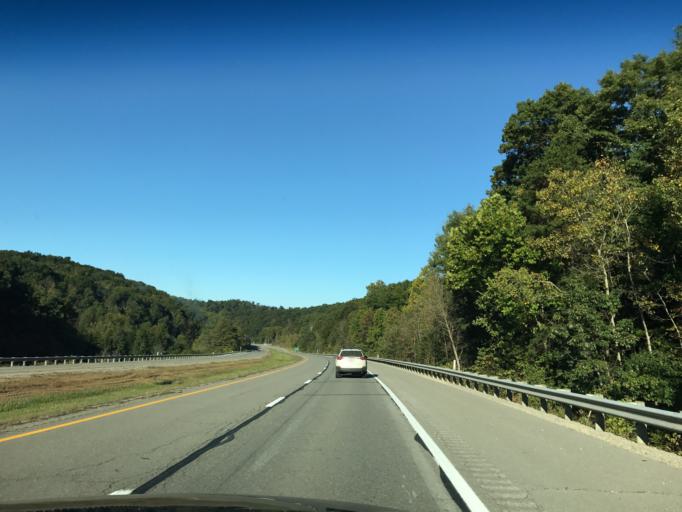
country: US
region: Ohio
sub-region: Washington County
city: Newport
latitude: 39.2589
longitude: -81.2803
